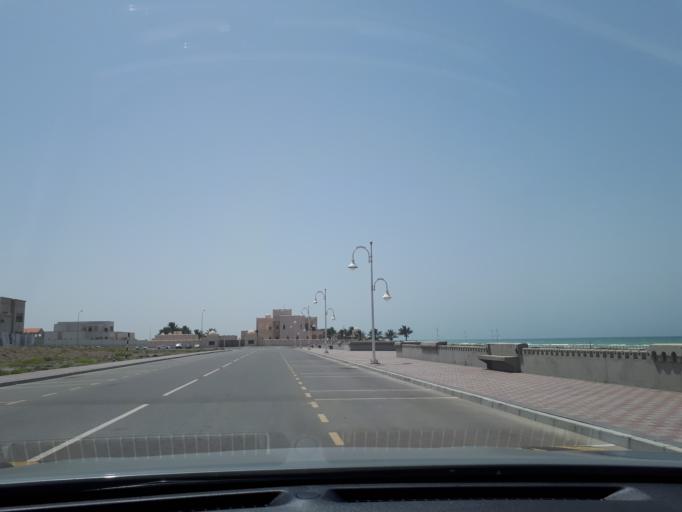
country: OM
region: Muhafazat Masqat
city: As Sib al Jadidah
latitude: 23.7124
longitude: 58.0677
